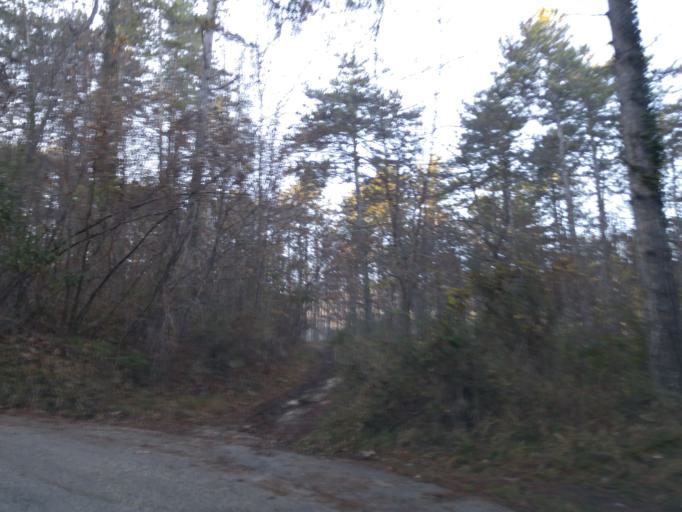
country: IT
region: The Marches
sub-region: Provincia di Pesaro e Urbino
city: Fossombrone
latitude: 43.6983
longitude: 12.7933
